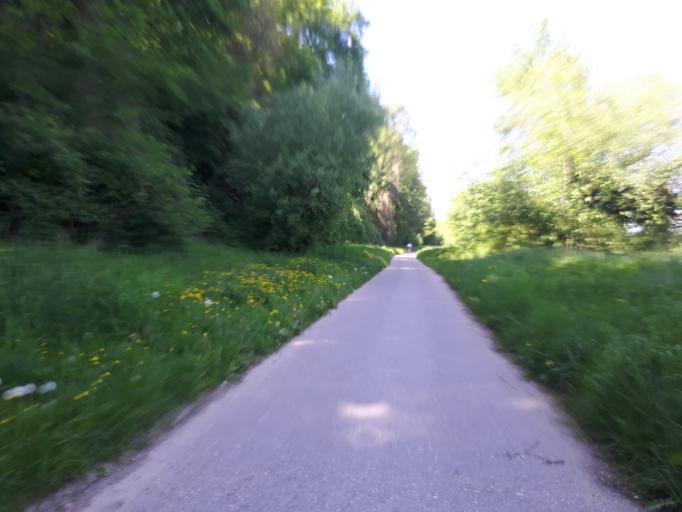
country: DE
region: Baden-Wuerttemberg
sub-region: Regierungsbezirk Stuttgart
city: Bad Wimpfen
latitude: 49.2374
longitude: 9.1575
